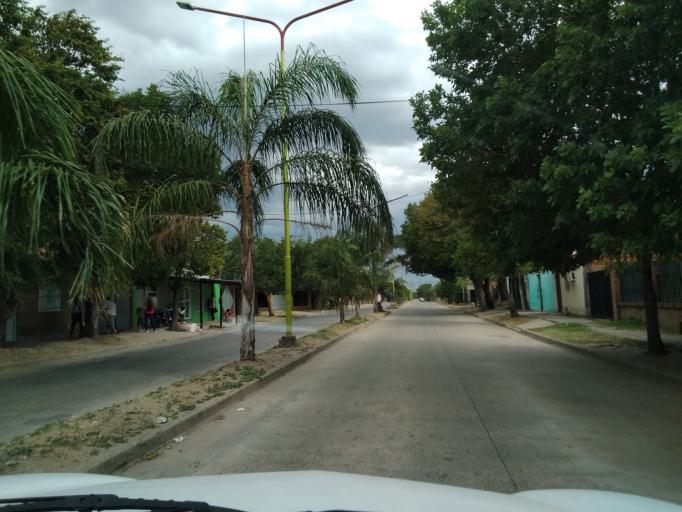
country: AR
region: Corrientes
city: Corrientes
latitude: -27.5216
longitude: -58.7912
